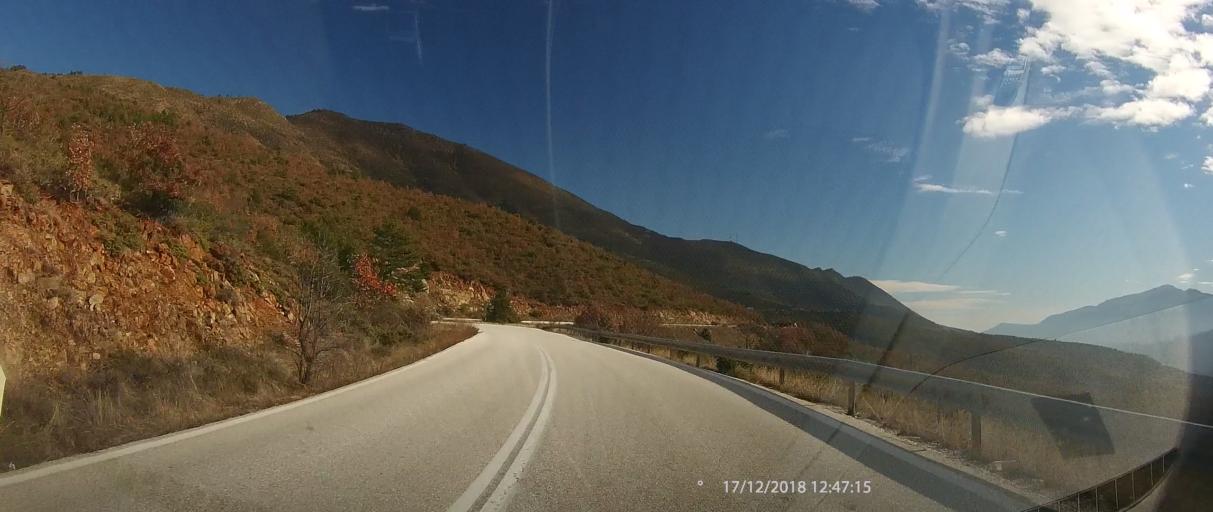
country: GR
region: Thessaly
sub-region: Trikala
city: Kastraki
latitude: 39.7855
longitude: 21.4253
